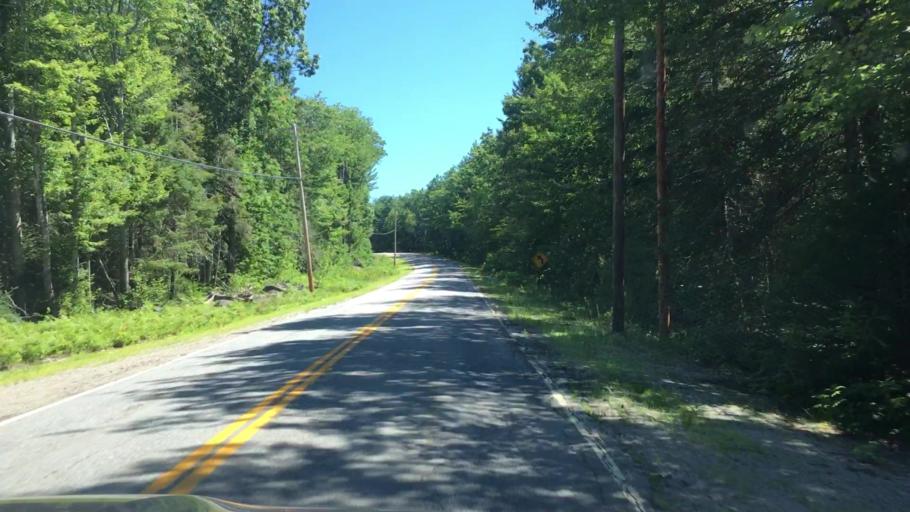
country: US
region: Maine
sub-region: Hancock County
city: Penobscot
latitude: 44.4739
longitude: -68.6988
